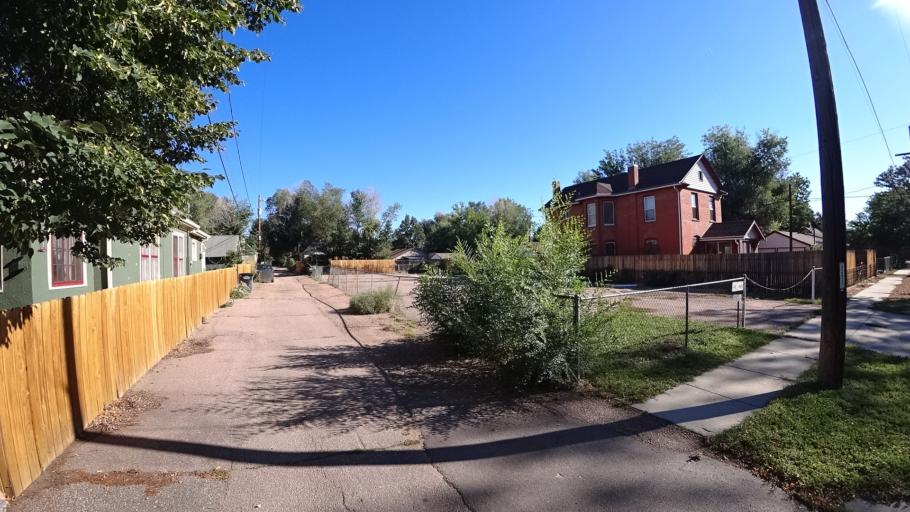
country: US
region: Colorado
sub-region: El Paso County
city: Colorado Springs
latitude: 38.8427
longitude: -104.8317
